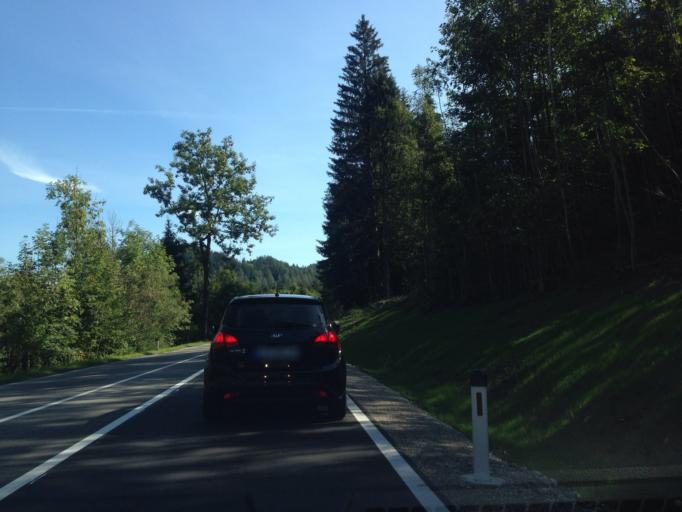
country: DE
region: Bavaria
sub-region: Swabia
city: Fuessen
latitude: 47.5571
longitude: 10.6894
